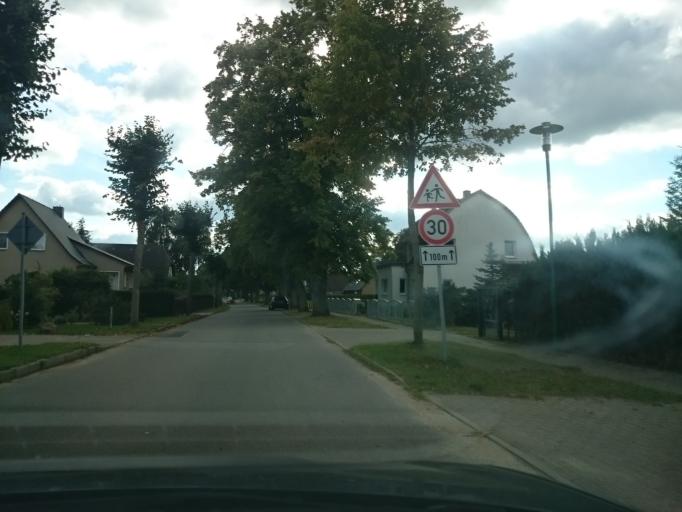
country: DE
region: Mecklenburg-Vorpommern
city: Carpin
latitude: 53.3609
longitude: 13.2474
